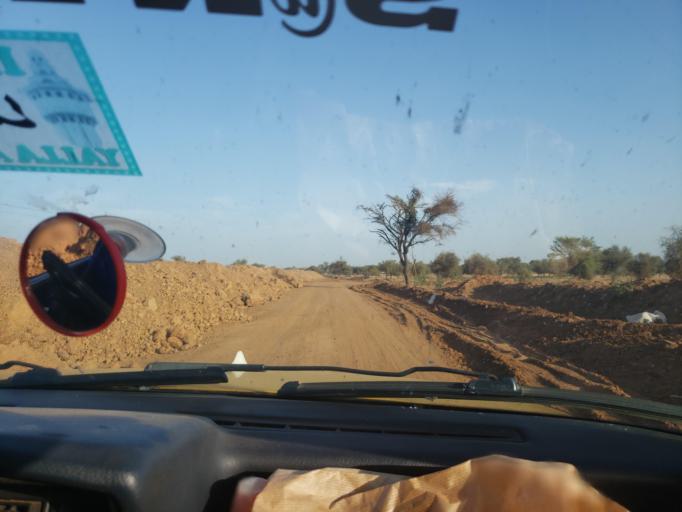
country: SN
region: Louga
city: Dara
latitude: 15.4151
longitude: -15.7097
